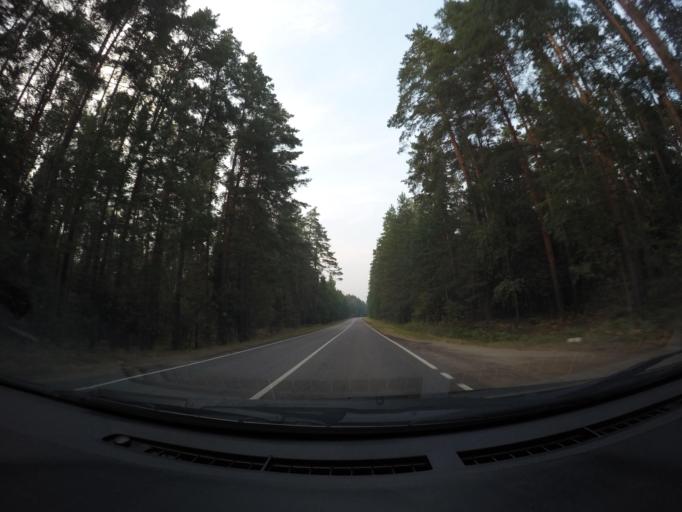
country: RU
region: Moskovskaya
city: Imeni Tsyurupy
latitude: 55.5074
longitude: 38.7158
